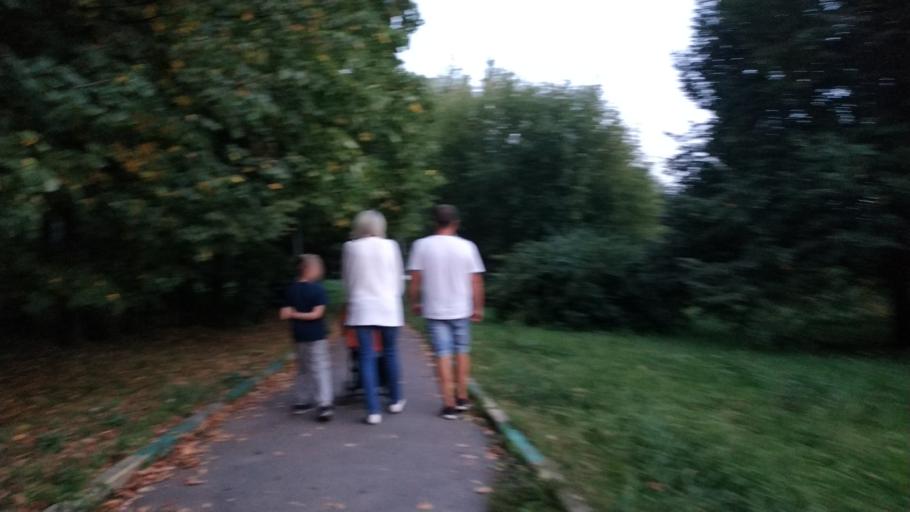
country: RU
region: Moscow
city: Solntsevo
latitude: 55.6366
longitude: 37.3776
